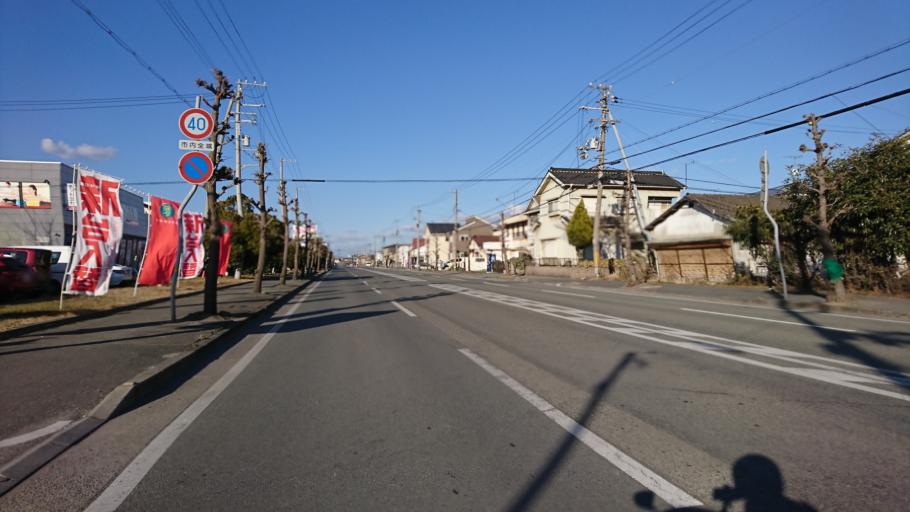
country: JP
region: Hyogo
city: Kakogawacho-honmachi
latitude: 34.7331
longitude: 134.8215
